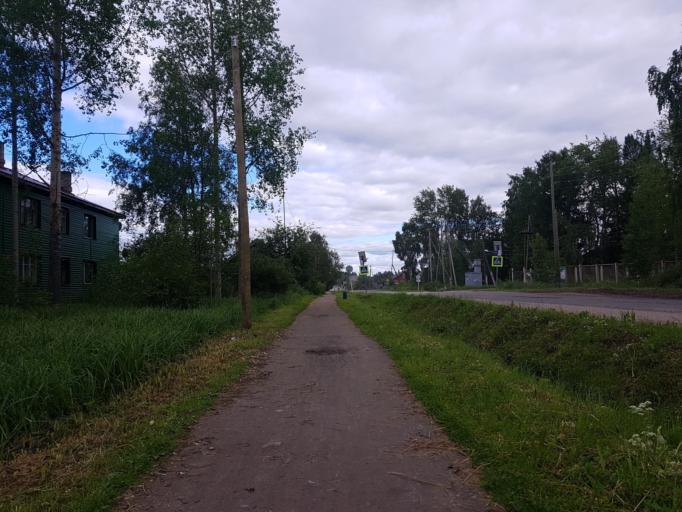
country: RU
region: Republic of Karelia
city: Kalevala
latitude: 65.2023
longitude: 31.1753
